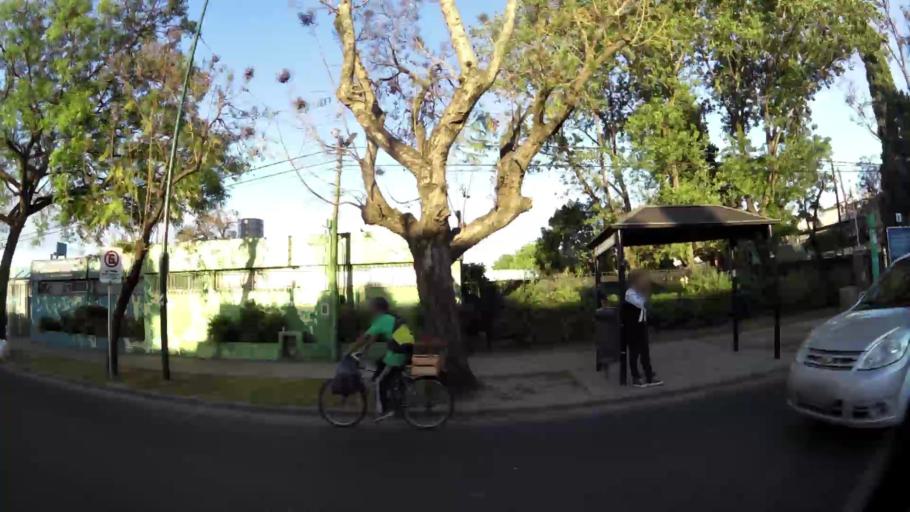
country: AR
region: Buenos Aires
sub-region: Partido de San Isidro
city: San Isidro
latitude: -34.4686
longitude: -58.5415
